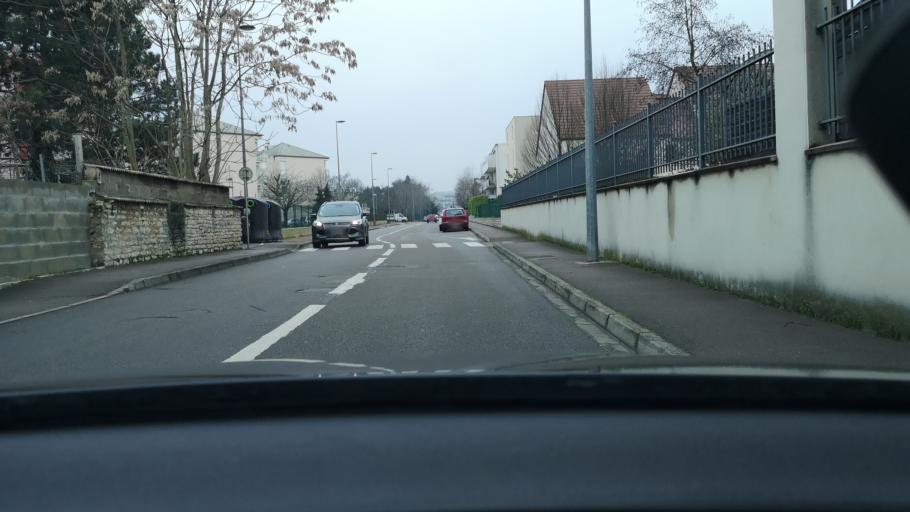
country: FR
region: Bourgogne
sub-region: Departement de Saone-et-Loire
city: Chalon-sur-Saone
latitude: 46.7953
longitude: 4.8563
